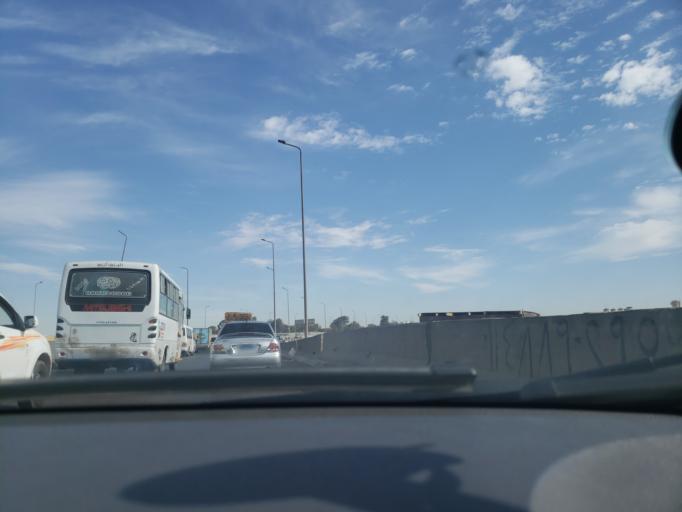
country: EG
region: Muhafazat al Qalyubiyah
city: Al Khankah
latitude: 30.1489
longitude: 31.4313
